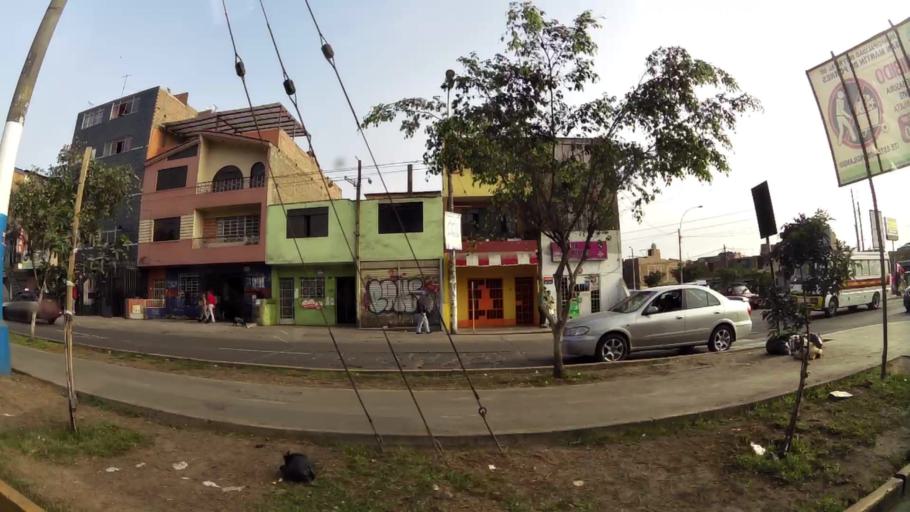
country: PE
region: Callao
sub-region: Callao
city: Callao
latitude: -12.0217
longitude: -77.0859
